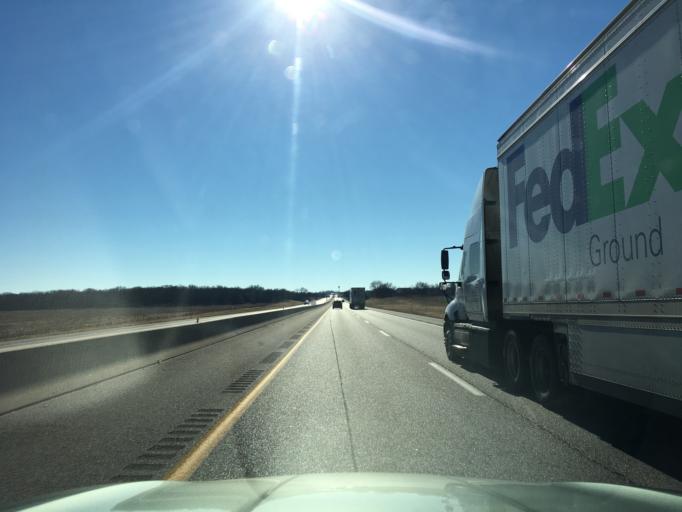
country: US
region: Kansas
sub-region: Sumner County
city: Belle Plaine
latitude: 37.3907
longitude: -97.3255
